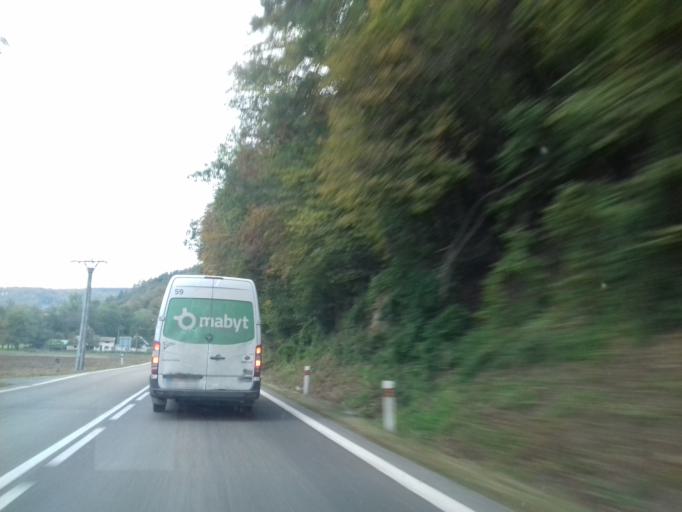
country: SK
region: Trenciansky
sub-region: Okres Trencin
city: Trencin
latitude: 48.9355
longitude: 17.9405
